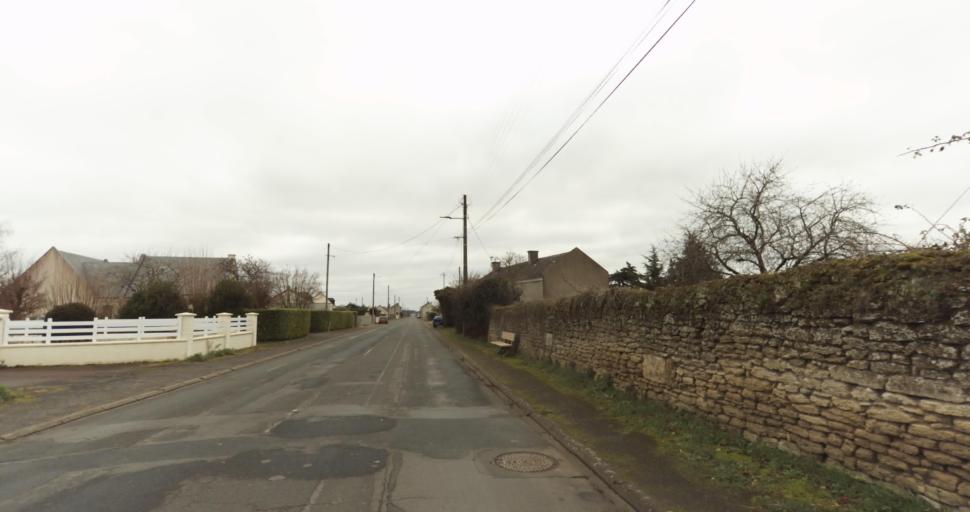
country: FR
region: Pays de la Loire
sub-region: Departement de Maine-et-Loire
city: Doue-la-Fontaine
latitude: 47.1879
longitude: -0.2602
